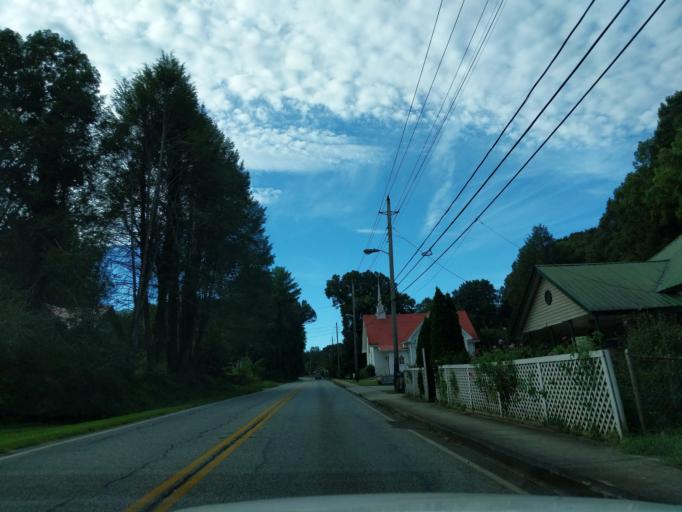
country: US
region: Georgia
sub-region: Fannin County
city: McCaysville
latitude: 34.9802
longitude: -84.3737
